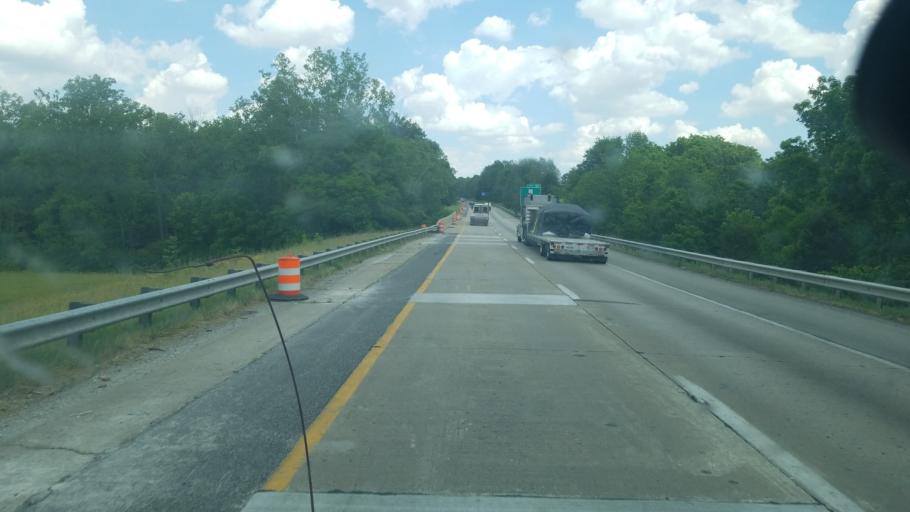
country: US
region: Indiana
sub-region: Henry County
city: Knightstown
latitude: 39.8529
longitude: -85.4426
